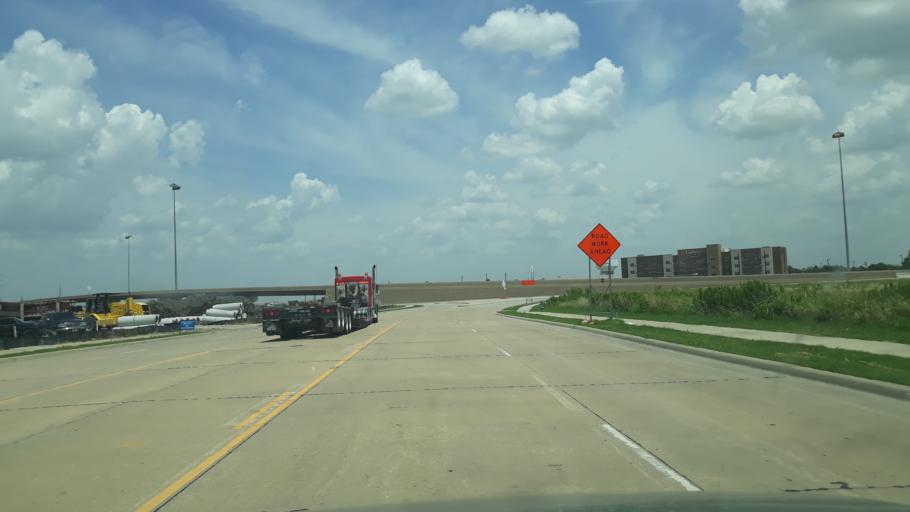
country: US
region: Texas
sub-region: Dallas County
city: Coppell
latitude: 32.9700
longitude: -97.0343
